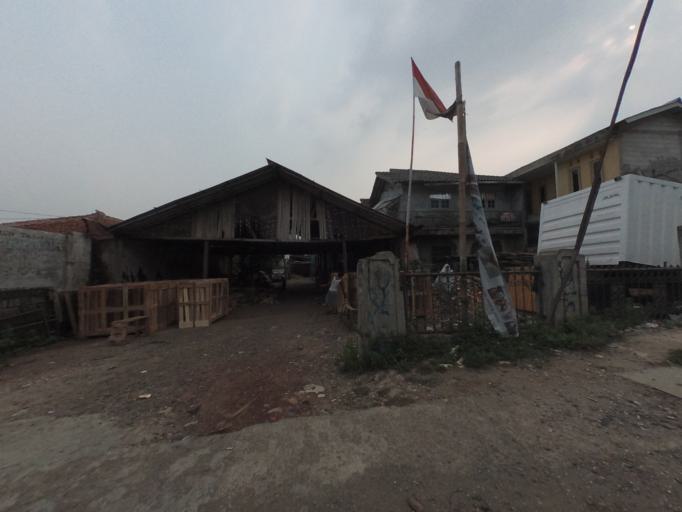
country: ID
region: West Java
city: Sidoger Lebak
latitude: -6.5664
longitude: 106.5951
